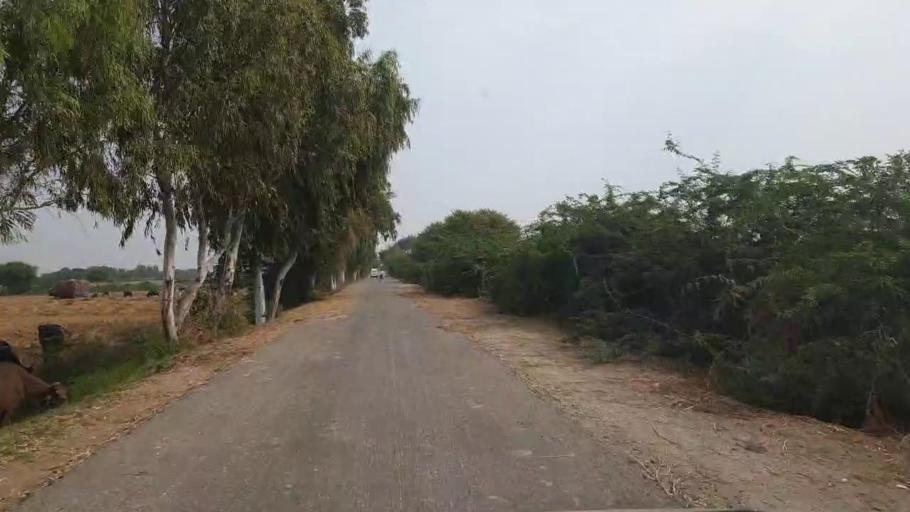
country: PK
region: Sindh
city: Talhar
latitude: 24.8940
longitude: 68.7986
